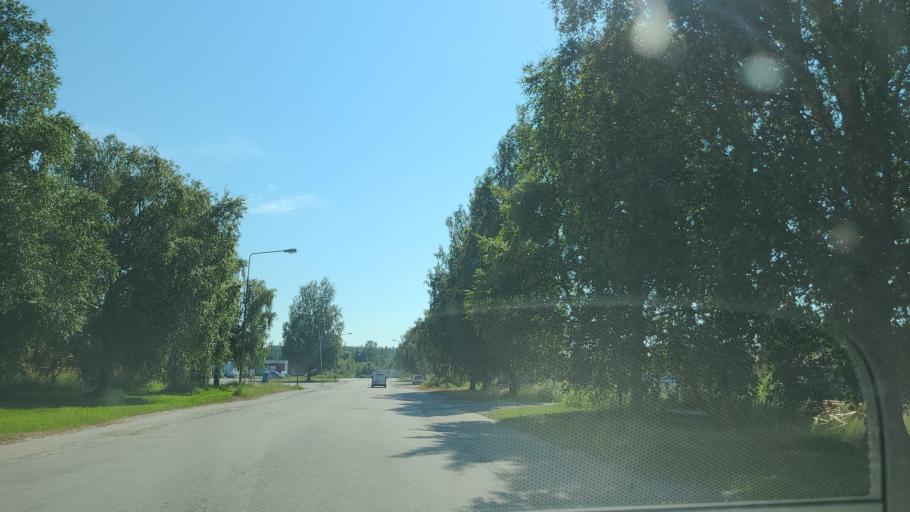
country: SE
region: Vaesterbotten
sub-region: Umea Kommun
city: Umea
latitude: 63.8435
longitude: 20.2256
